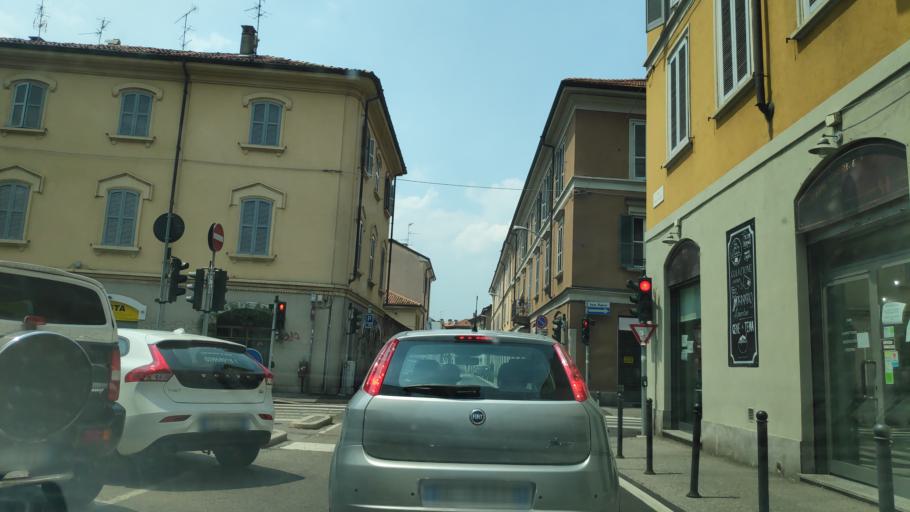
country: IT
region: Lombardy
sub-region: Provincia di Monza e Brianza
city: Monza
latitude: 45.5878
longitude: 9.2726
